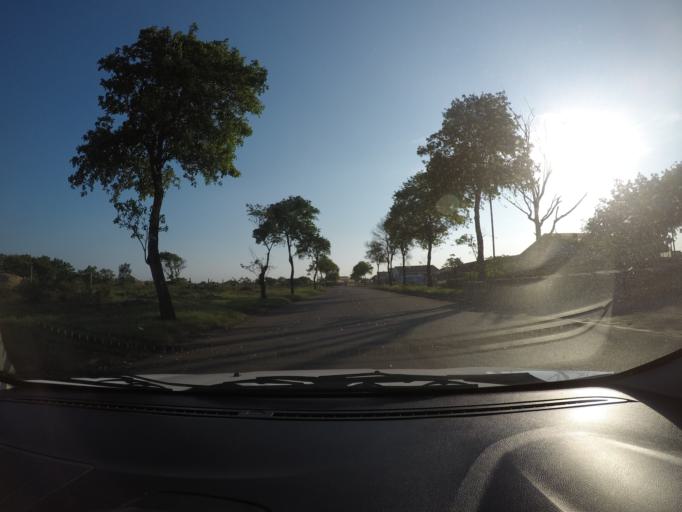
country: ZA
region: KwaZulu-Natal
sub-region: uThungulu District Municipality
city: Richards Bay
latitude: -28.7606
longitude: 32.0080
